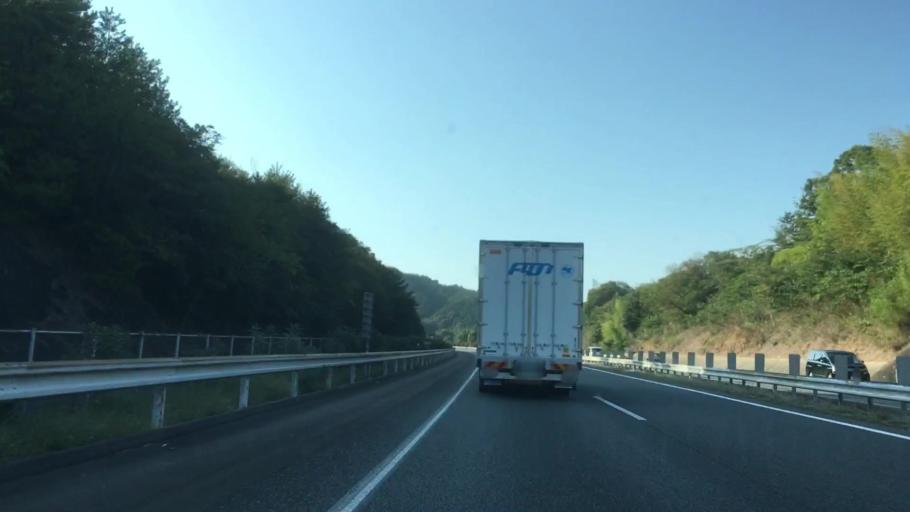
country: JP
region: Yamaguchi
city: Hofu
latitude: 34.0747
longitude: 131.4934
